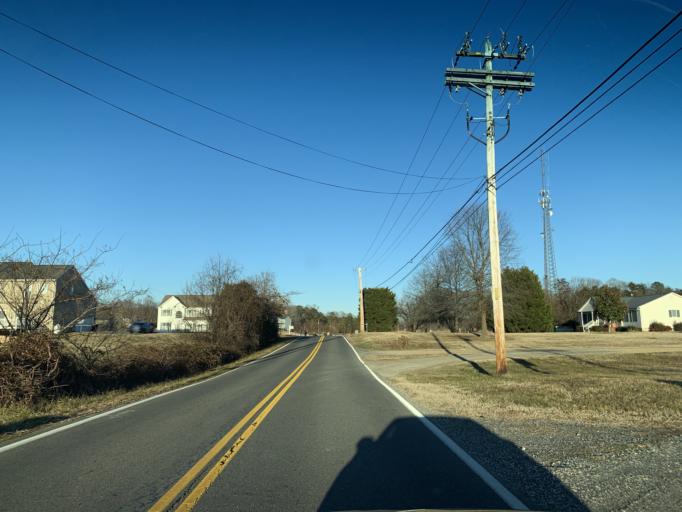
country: US
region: Maryland
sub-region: Saint Mary's County
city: Mechanicsville
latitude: 38.4434
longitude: -76.7298
